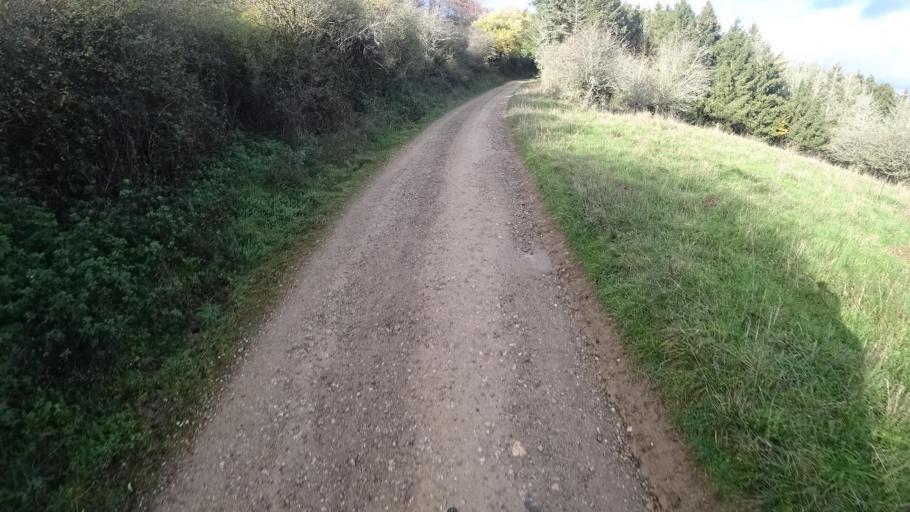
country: DE
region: Rheinland-Pfalz
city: Honningen
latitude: 50.4645
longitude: 6.9434
